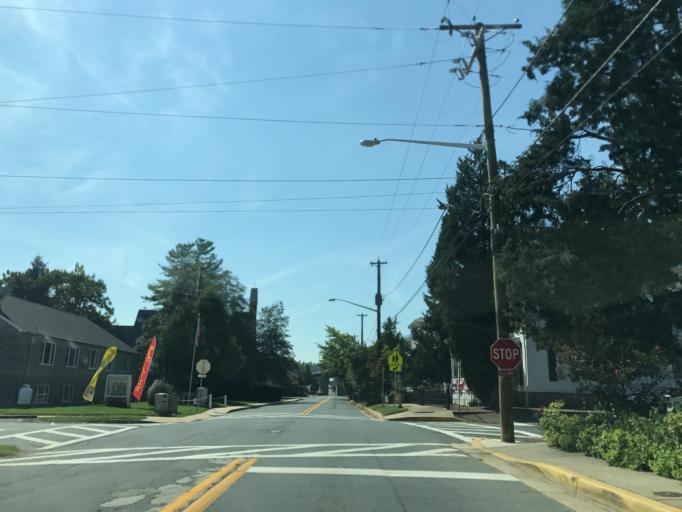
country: US
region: Maryland
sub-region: Cecil County
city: Elkton
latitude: 39.5268
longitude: -75.8139
